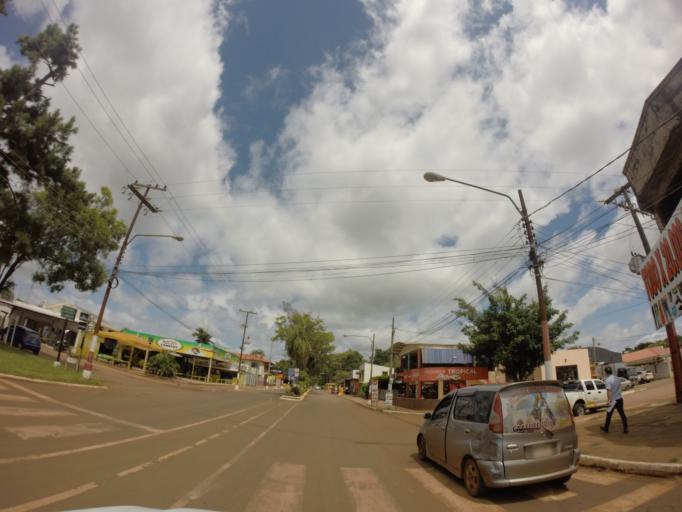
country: PY
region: Alto Parana
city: Ciudad del Este
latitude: -25.4061
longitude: -54.6398
